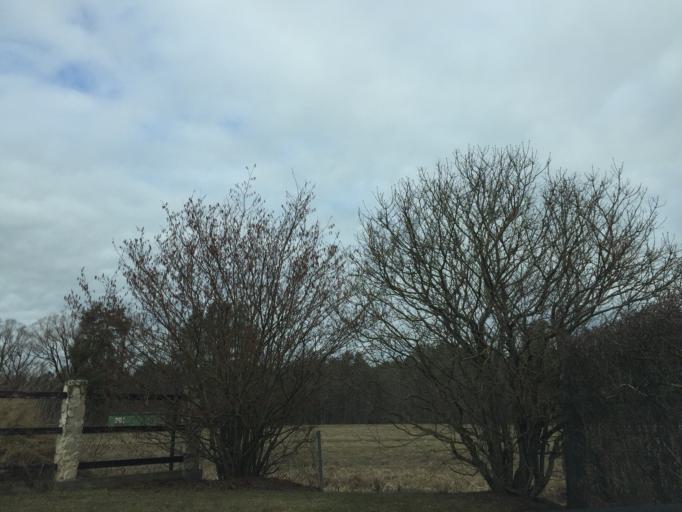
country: LV
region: Garkalne
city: Garkalne
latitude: 57.0741
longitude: 24.4235
